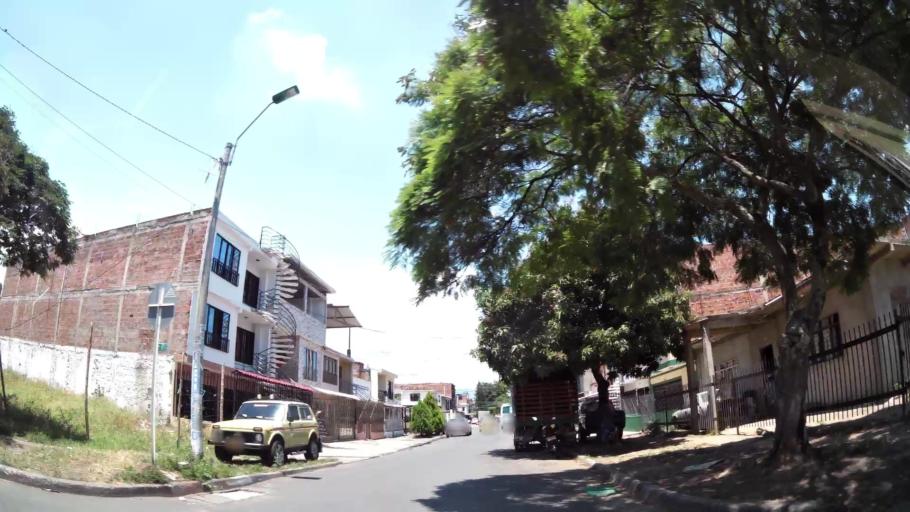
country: CO
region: Valle del Cauca
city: Cali
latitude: 3.4312
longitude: -76.5054
